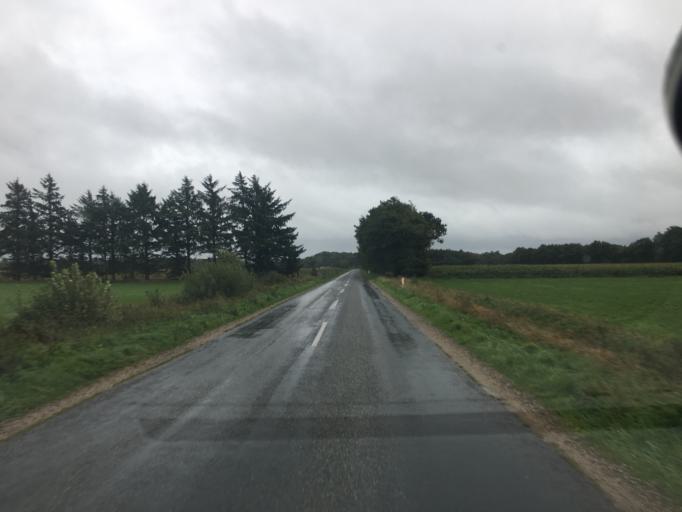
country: DE
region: Schleswig-Holstein
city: Bramstedtlund
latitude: 54.9641
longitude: 9.0493
